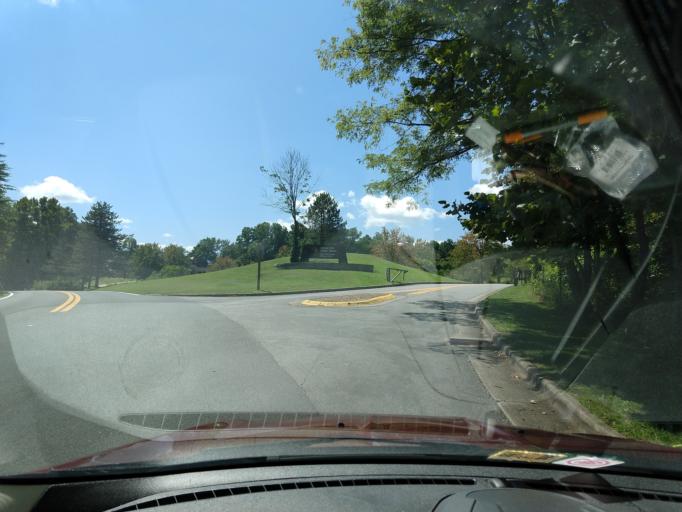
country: US
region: West Virginia
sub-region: Fayette County
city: Fayetteville
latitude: 38.0718
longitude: -81.0749
